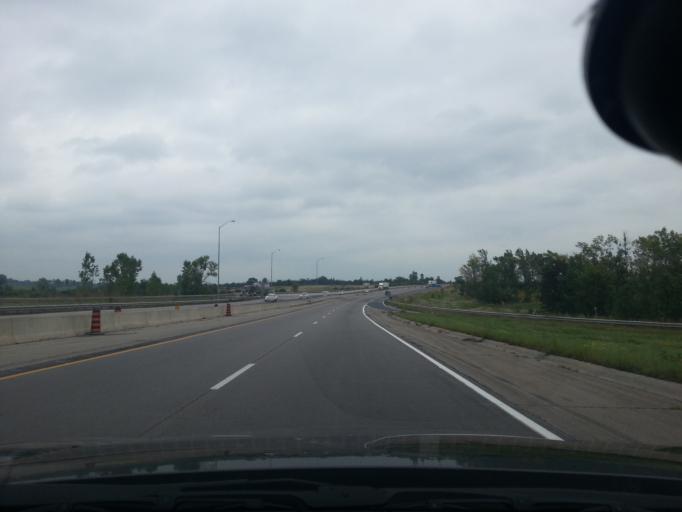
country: CA
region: Ontario
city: Greater Napanee
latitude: 44.2653
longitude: -76.9633
